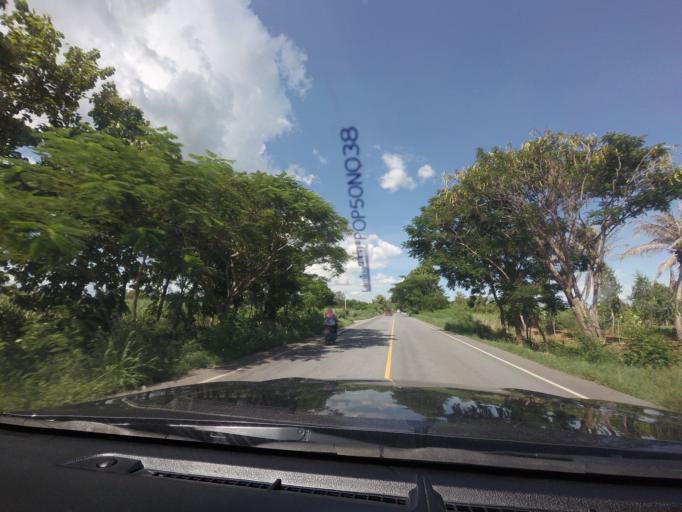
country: TH
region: Kanchanaburi
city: Phanom Thuan
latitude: 14.1761
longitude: 99.7836
